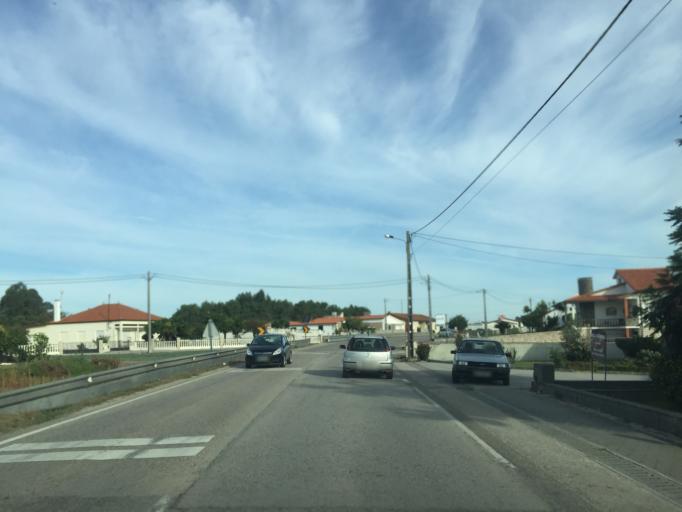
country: PT
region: Leiria
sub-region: Pombal
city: Lourical
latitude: 39.9780
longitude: -8.7987
